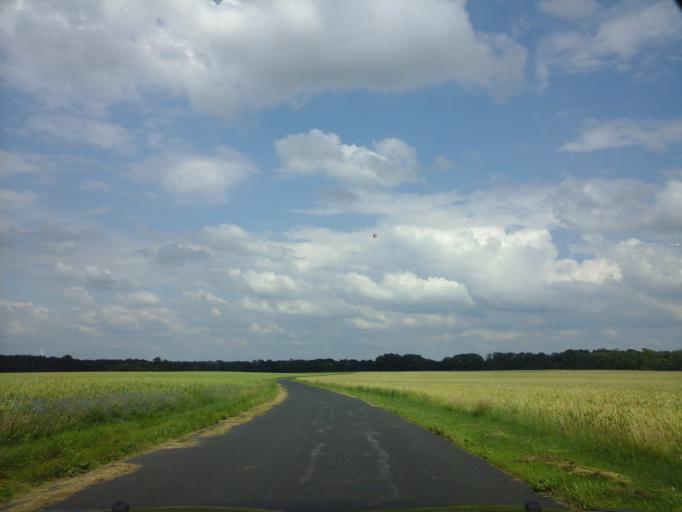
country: PL
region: West Pomeranian Voivodeship
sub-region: Powiat choszczenski
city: Pelczyce
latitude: 53.0873
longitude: 15.3756
